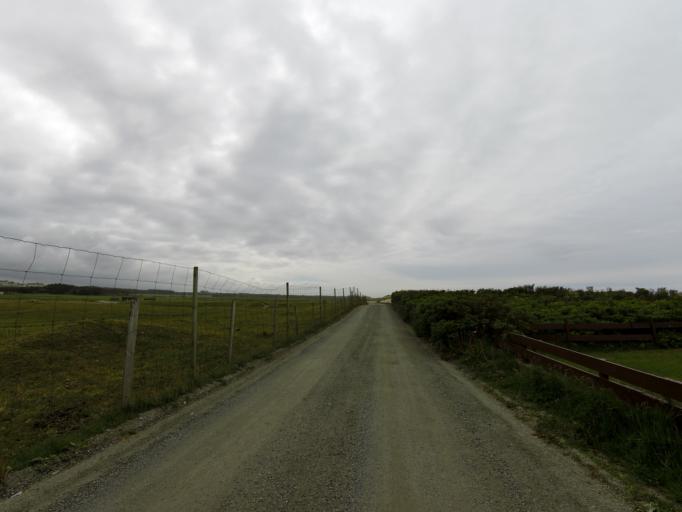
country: NO
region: Rogaland
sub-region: Klepp
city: Kleppe
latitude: 58.8011
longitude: 5.5518
